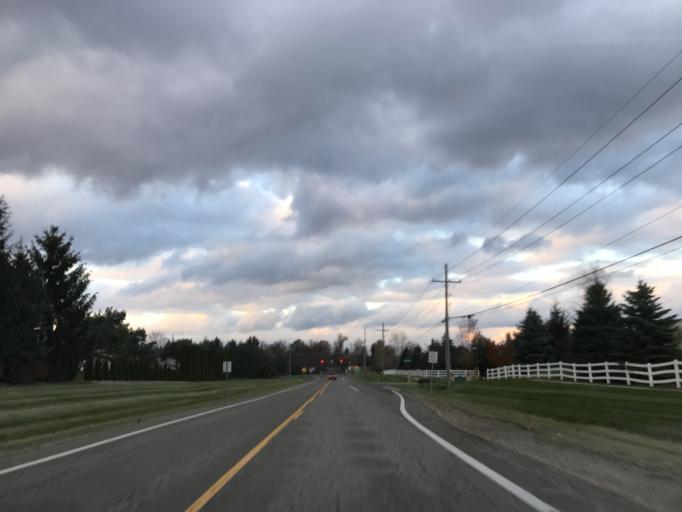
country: US
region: Michigan
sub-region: Oakland County
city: South Lyon
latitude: 42.4733
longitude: -83.6374
